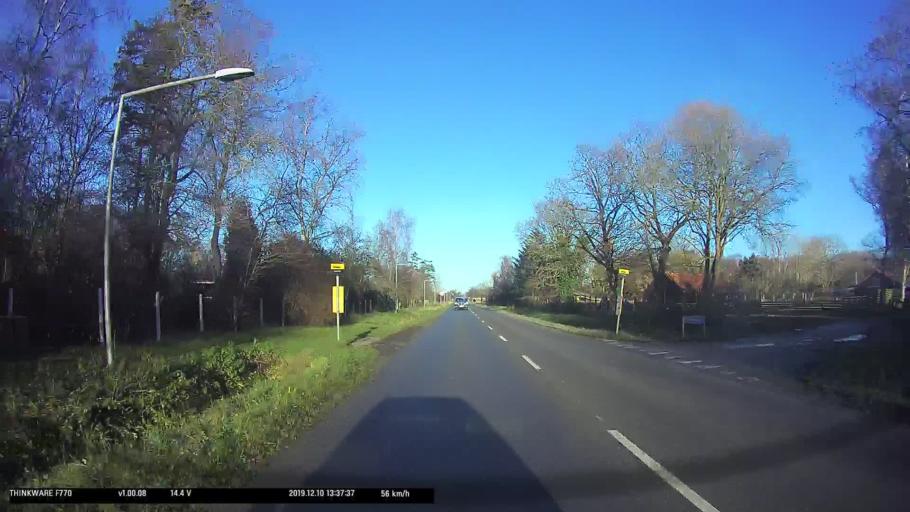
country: DK
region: Capital Region
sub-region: Tarnby Kommune
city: Tarnby
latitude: 55.5855
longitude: 12.5792
